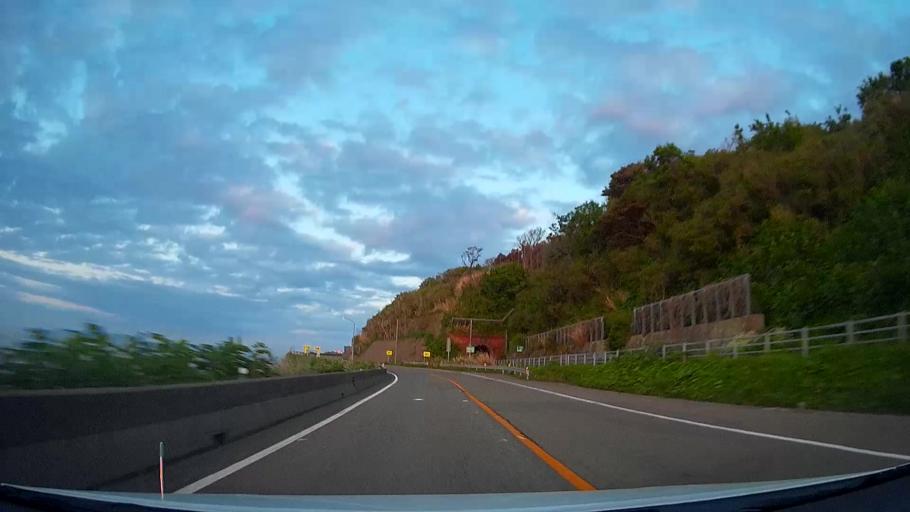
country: JP
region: Niigata
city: Joetsu
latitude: 37.1707
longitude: 138.1161
